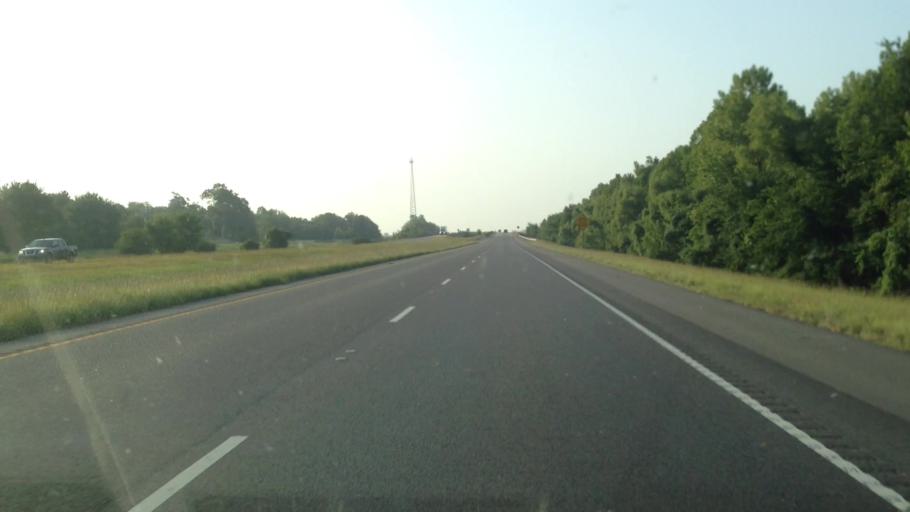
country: US
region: Louisiana
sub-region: Rapides Parish
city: Boyce
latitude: 31.3969
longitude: -92.6994
